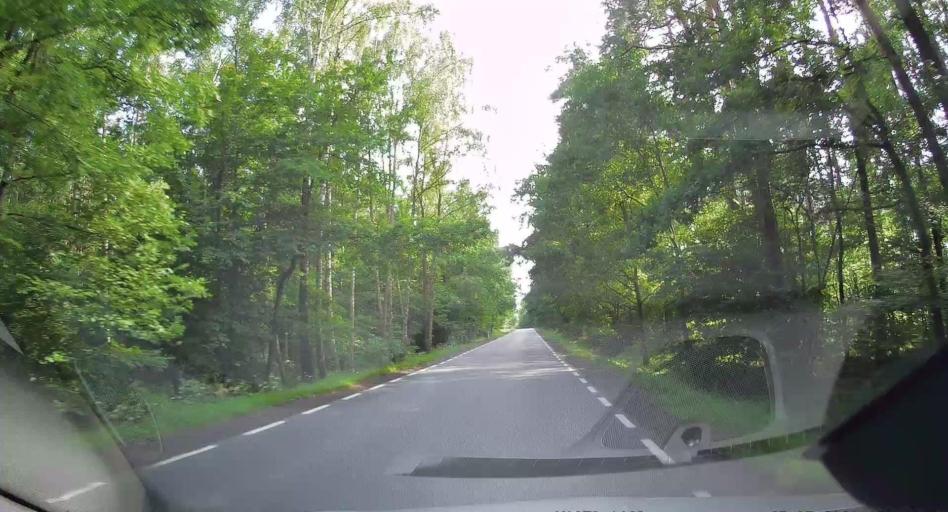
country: PL
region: Lodz Voivodeship
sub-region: Powiat tomaszowski
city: Rzeczyca
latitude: 51.5707
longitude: 20.2762
